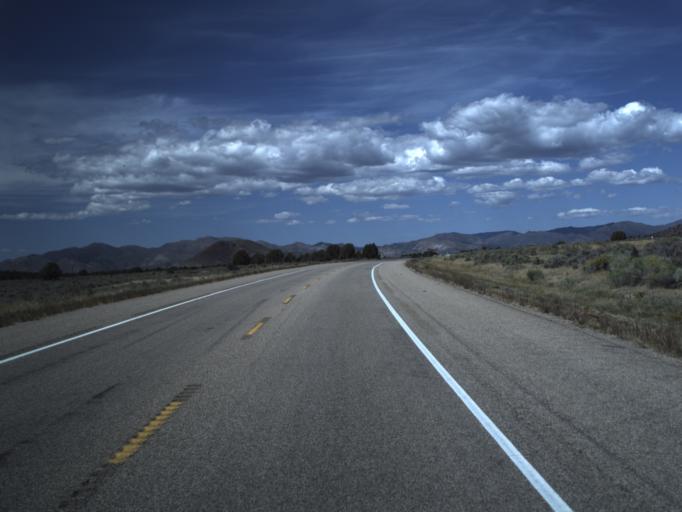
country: US
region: Utah
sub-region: Washington County
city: Ivins
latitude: 37.2780
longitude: -113.6507
